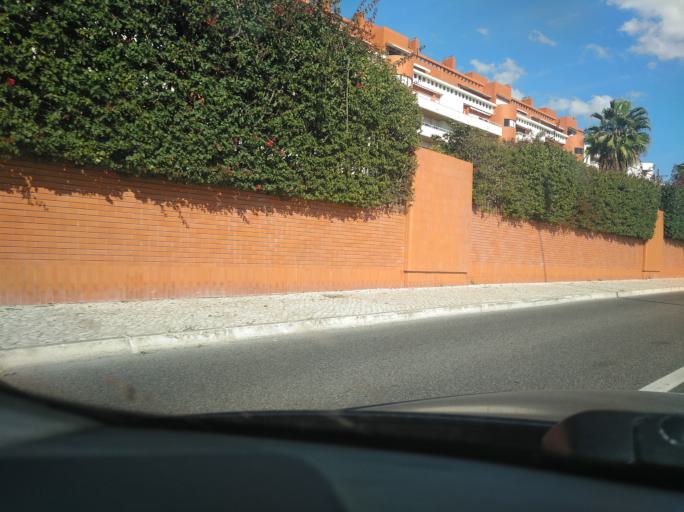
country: PT
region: Lisbon
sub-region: Oeiras
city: Alges
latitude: 38.7039
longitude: -9.2341
